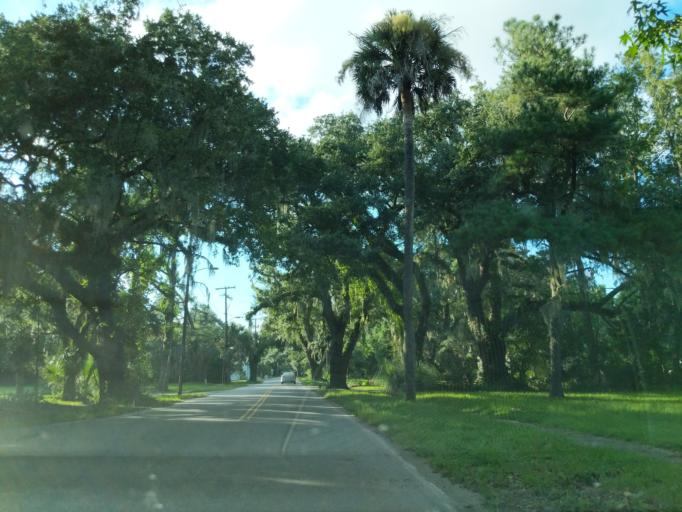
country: US
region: South Carolina
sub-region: Charleston County
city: Awendaw
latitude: 33.0881
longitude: -79.4611
